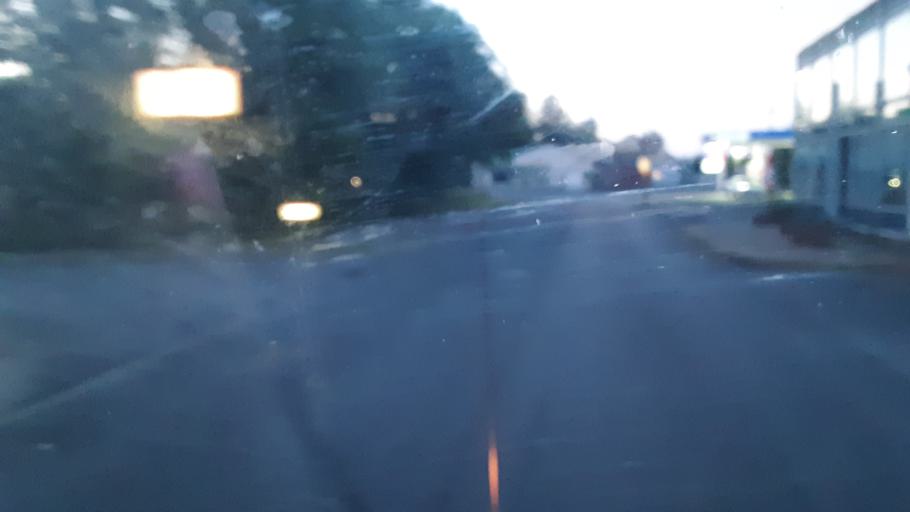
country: US
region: New York
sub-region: Montgomery County
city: Amsterdam
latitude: 42.9375
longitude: -74.1795
